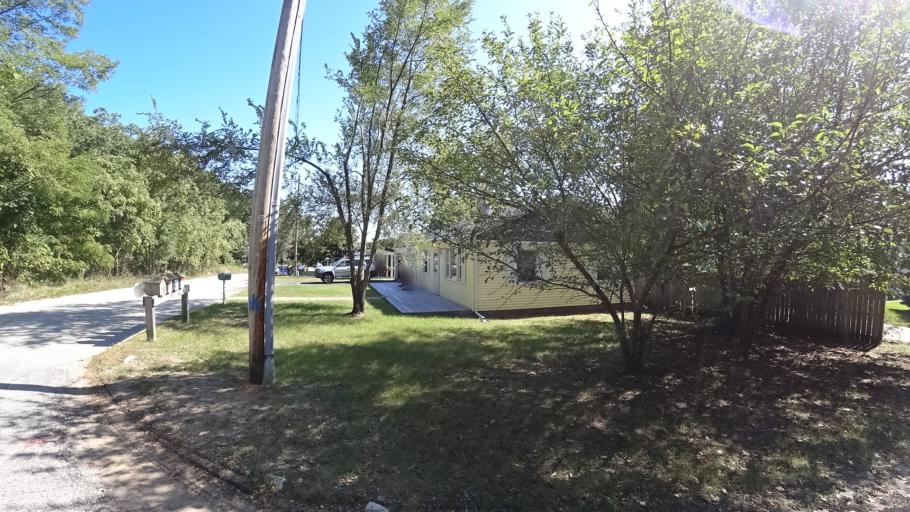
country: US
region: Indiana
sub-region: LaPorte County
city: Michigan City
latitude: 41.7289
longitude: -86.8885
